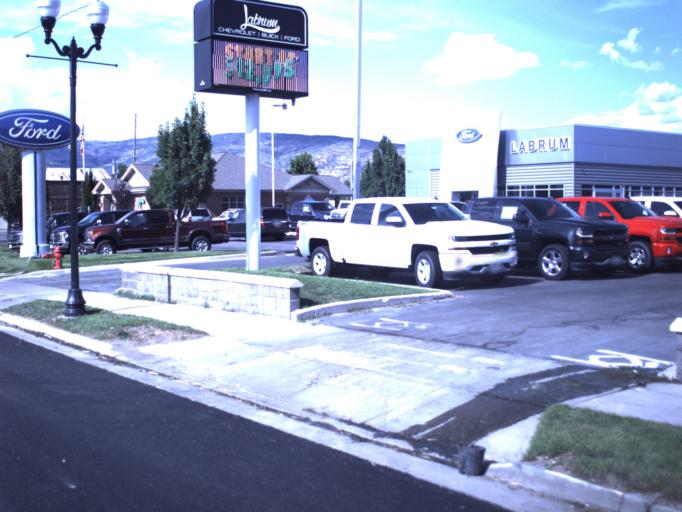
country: US
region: Utah
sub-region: Wasatch County
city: Heber
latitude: 40.4952
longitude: -111.4135
